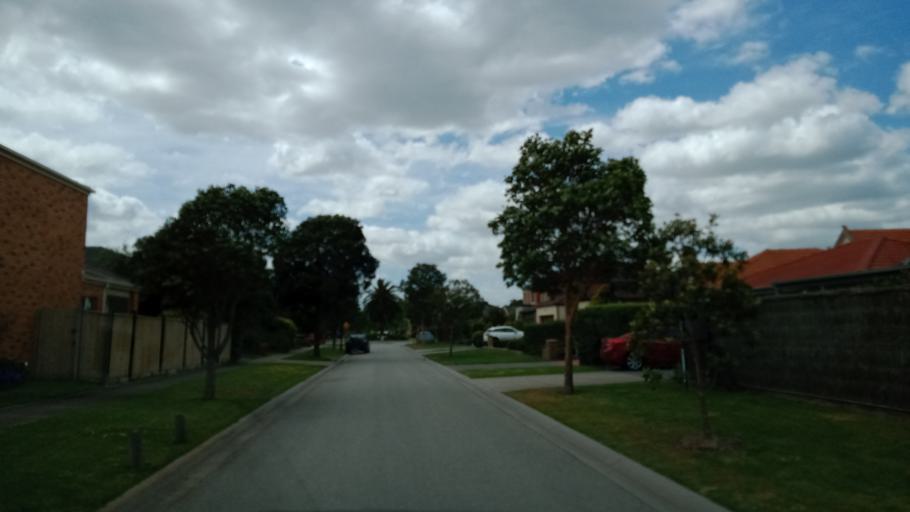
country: AU
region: Victoria
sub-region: Kingston
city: Patterson Lakes
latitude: -38.0567
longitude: 145.1387
